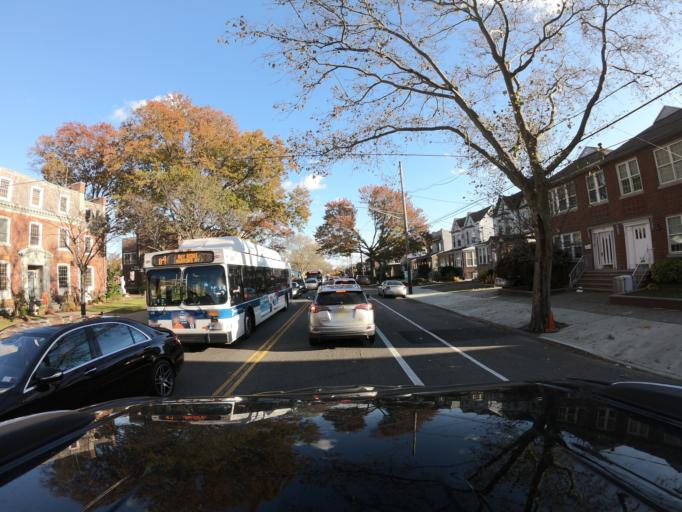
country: US
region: New York
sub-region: Kings County
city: Bensonhurst
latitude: 40.6253
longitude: -74.0158
